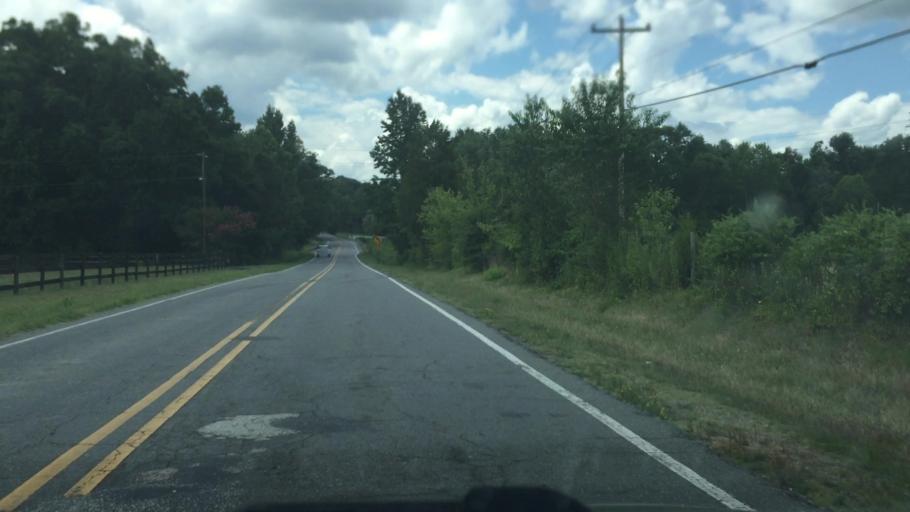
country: US
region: North Carolina
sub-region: Rowan County
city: Enochville
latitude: 35.4808
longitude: -80.7279
